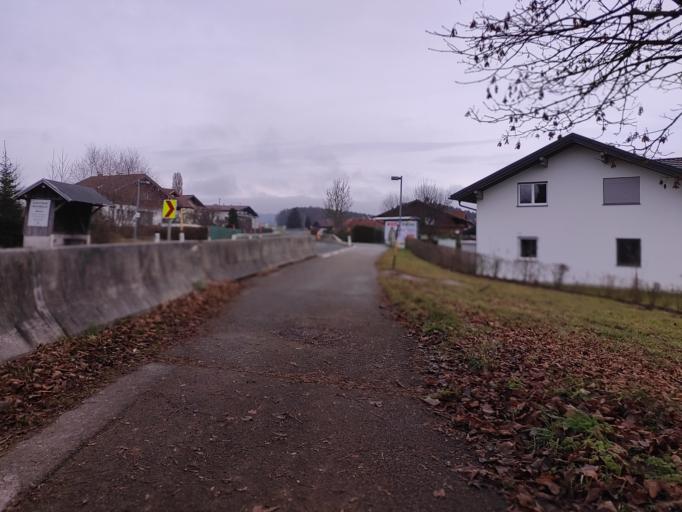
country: AT
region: Salzburg
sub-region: Politischer Bezirk Salzburg-Umgebung
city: Mattsee
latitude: 47.9888
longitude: 13.1124
